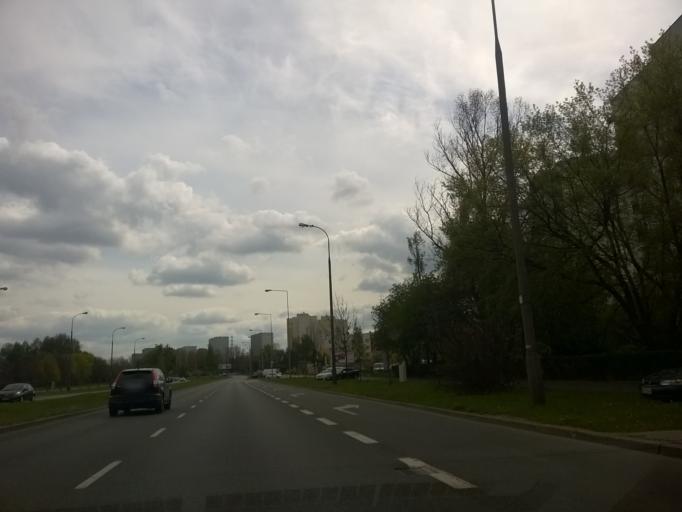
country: PL
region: Masovian Voivodeship
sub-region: Warszawa
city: Ursynow
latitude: 52.1593
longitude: 21.0408
